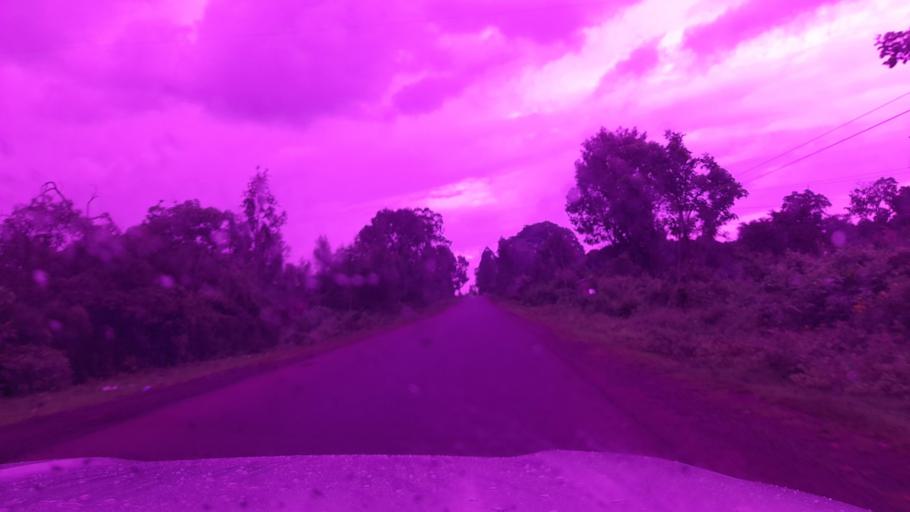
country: ET
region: Oromiya
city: Jima
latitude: 7.7086
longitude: 37.0565
